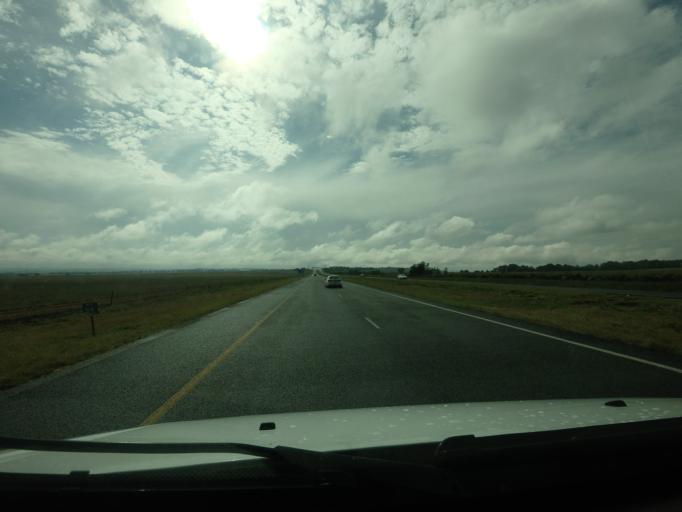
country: ZA
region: Gauteng
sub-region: City of Tshwane Metropolitan Municipality
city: Cullinan
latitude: -25.7976
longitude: 28.5332
